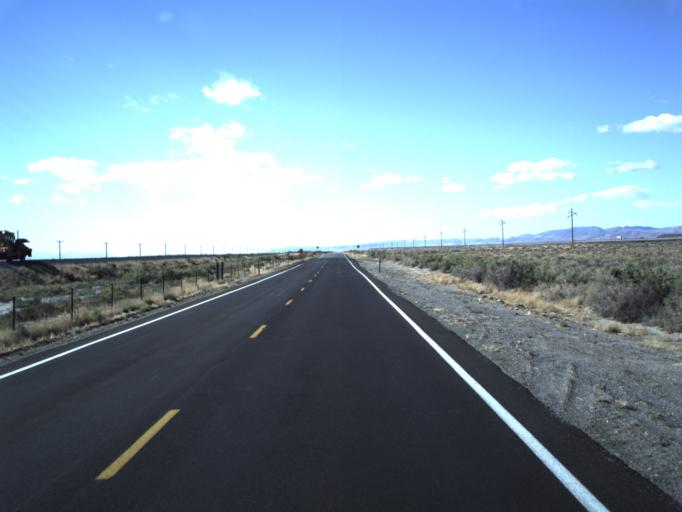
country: US
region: Utah
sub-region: Millard County
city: Delta
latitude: 39.2168
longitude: -112.6777
